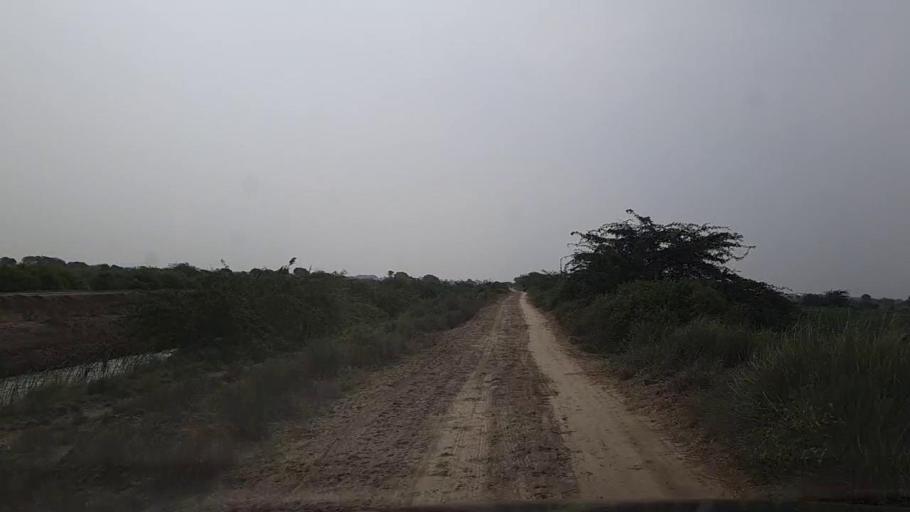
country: PK
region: Sindh
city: Thatta
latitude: 24.7540
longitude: 67.8087
